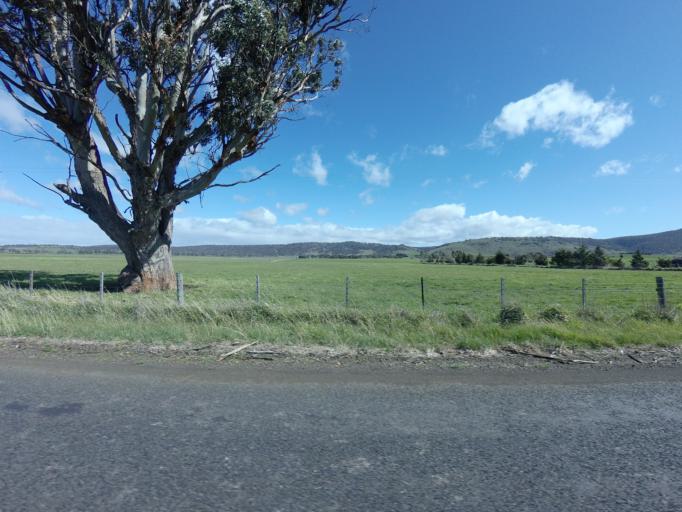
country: AU
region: Tasmania
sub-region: Northern Midlands
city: Evandale
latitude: -42.0101
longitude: 147.4592
